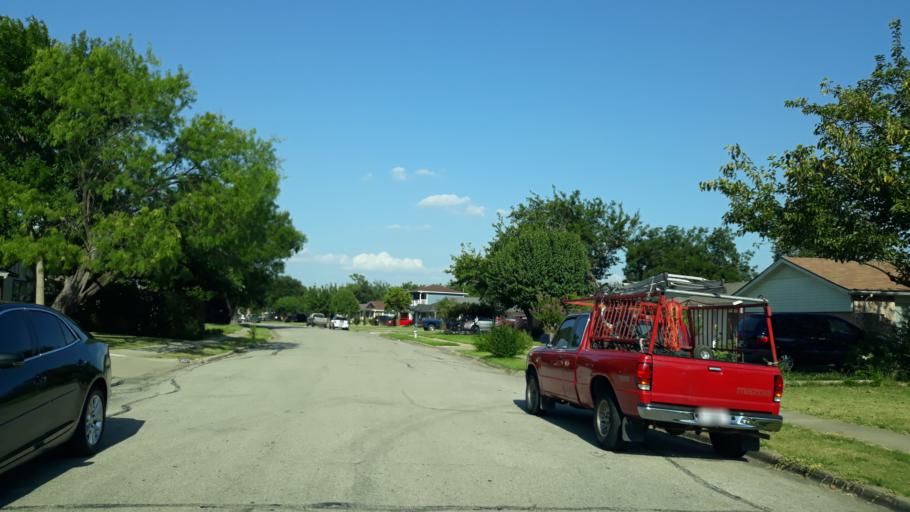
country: US
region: Texas
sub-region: Dallas County
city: Irving
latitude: 32.8402
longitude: -96.9791
